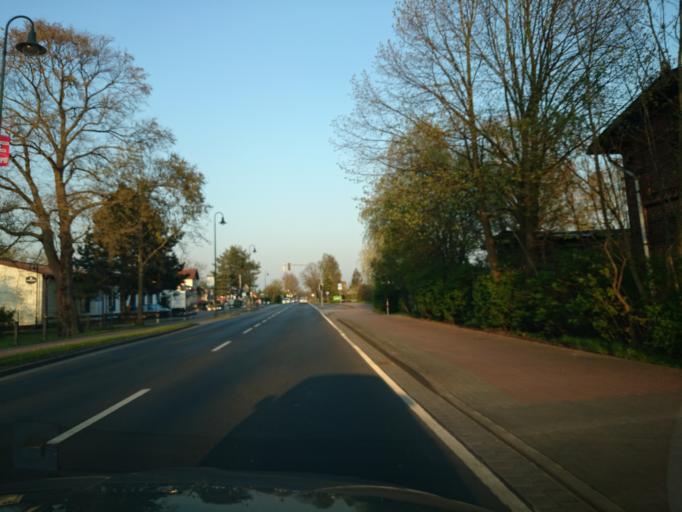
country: DE
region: Mecklenburg-Vorpommern
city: Broderstorf
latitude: 54.0793
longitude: 12.2614
